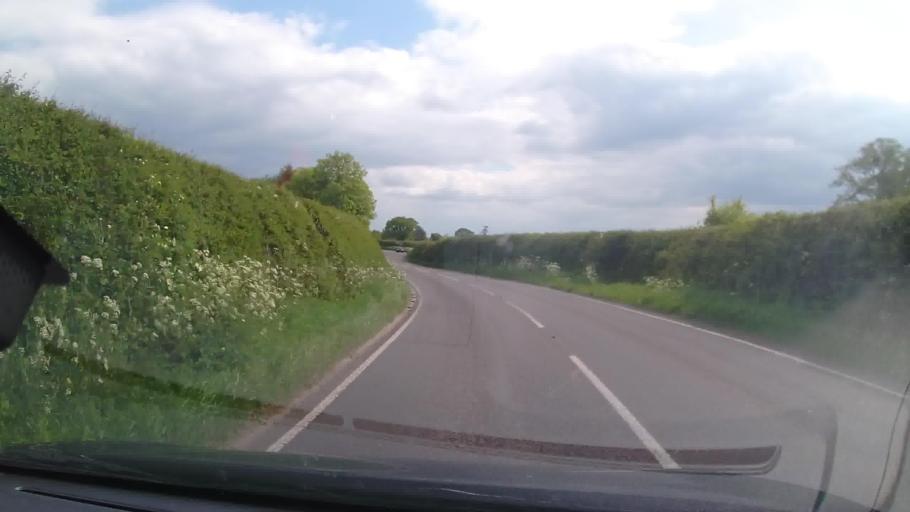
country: GB
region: England
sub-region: Shropshire
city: Whitchurch
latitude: 52.9525
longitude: -2.6800
